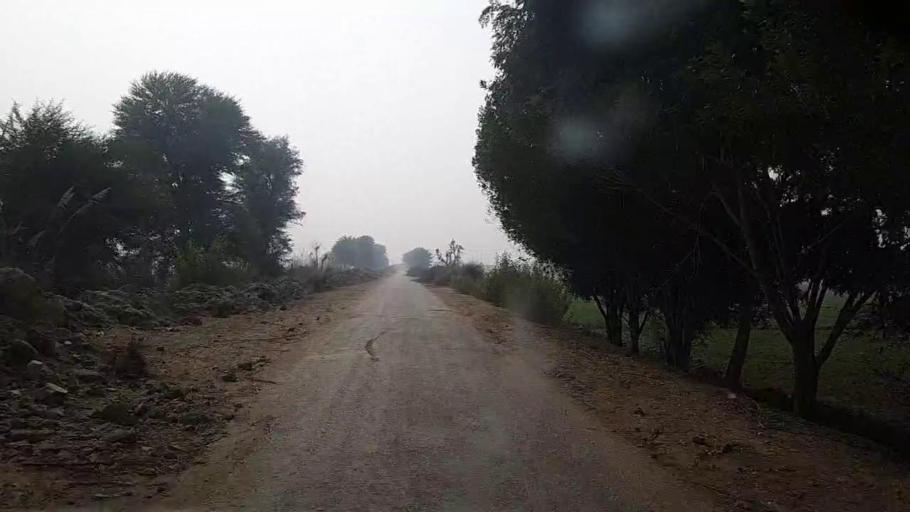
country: PK
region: Sindh
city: Kandiari
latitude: 26.9865
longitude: 68.6034
